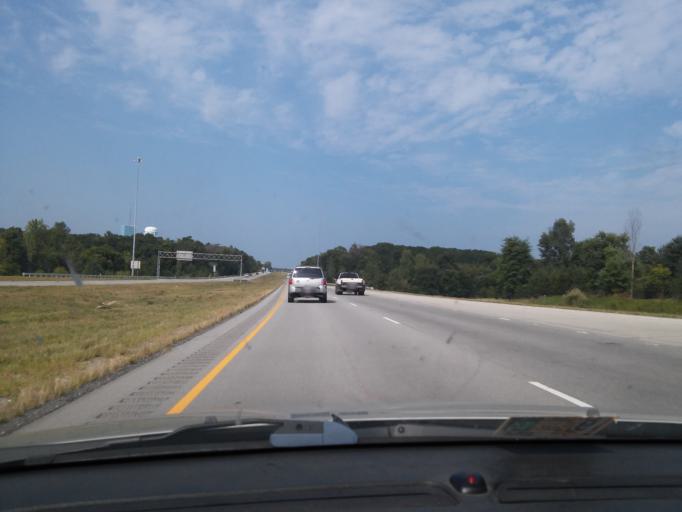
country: US
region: Ohio
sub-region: Greene County
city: Xenia
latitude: 39.6663
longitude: -83.9107
